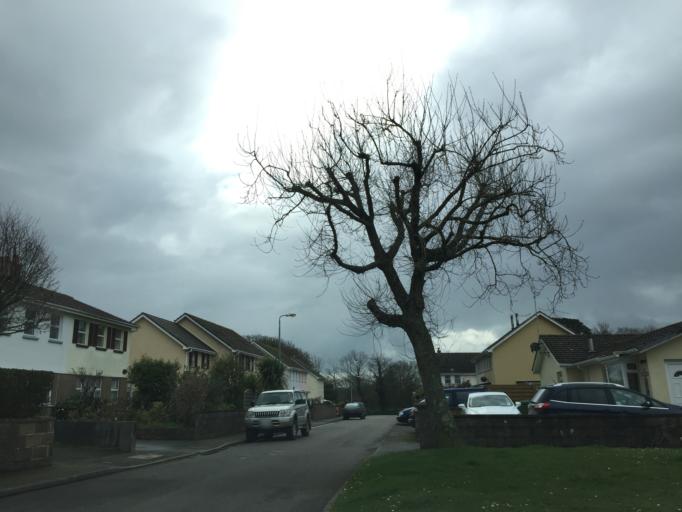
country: JE
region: St Helier
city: Saint Helier
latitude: 49.2356
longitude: -2.1776
